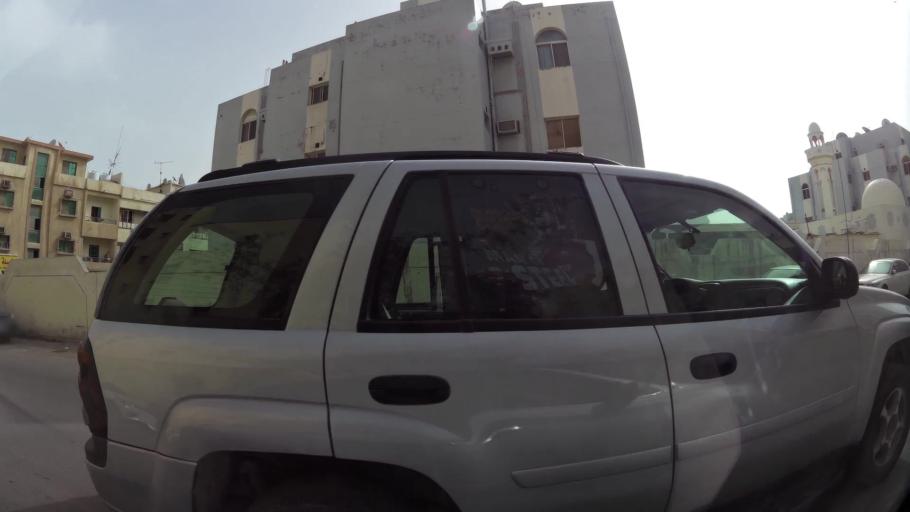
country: QA
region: Baladiyat ad Dawhah
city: Doha
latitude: 25.2763
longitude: 51.5501
